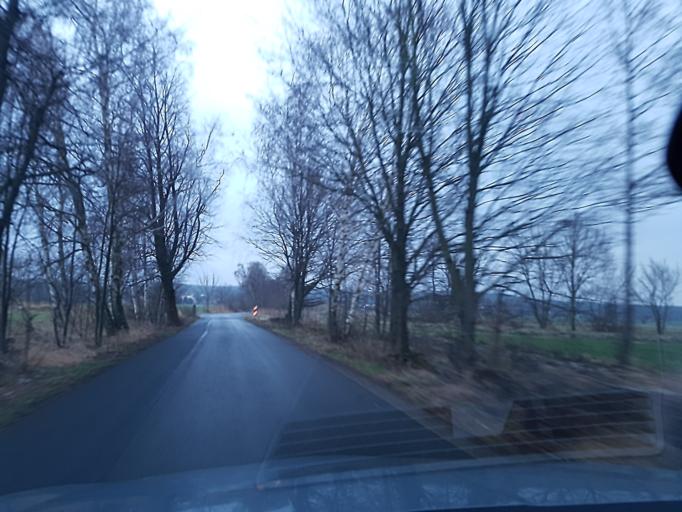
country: DE
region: Brandenburg
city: Groden
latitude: 51.4163
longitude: 13.5636
